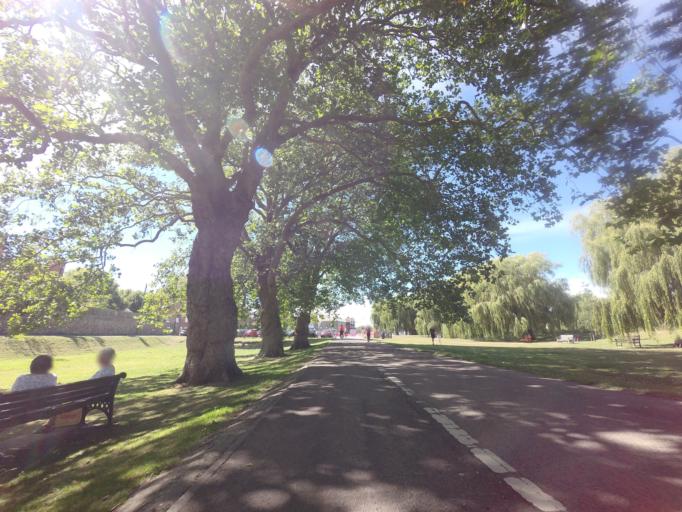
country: GB
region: England
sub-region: Kent
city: Sandwich
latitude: 51.2748
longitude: 1.3453
